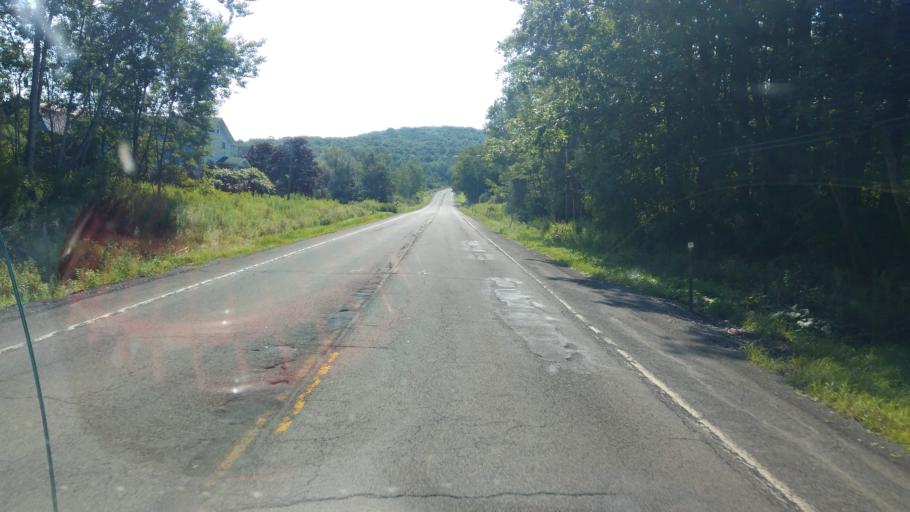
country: US
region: New York
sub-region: Allegany County
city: Cuba
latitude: 42.1746
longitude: -78.2507
